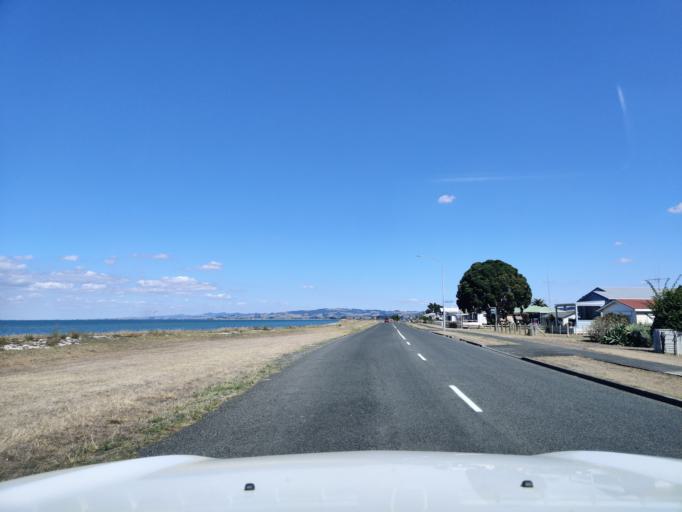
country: NZ
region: Waikato
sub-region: Thames-Coromandel District
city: Thames
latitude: -37.1060
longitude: 175.2993
